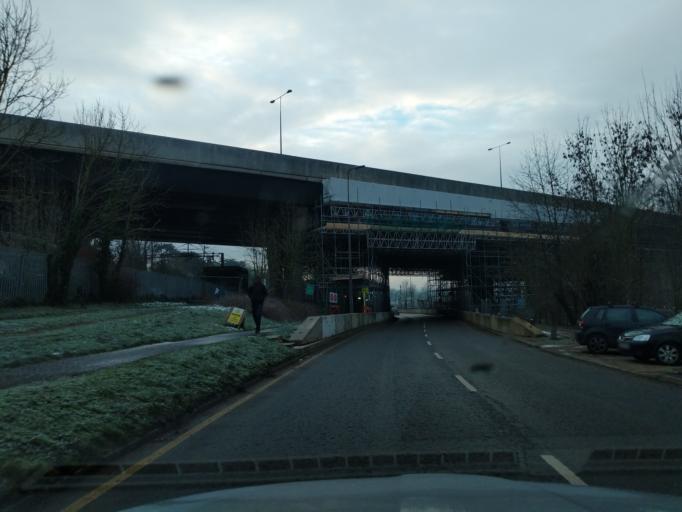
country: GB
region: England
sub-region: Hertfordshire
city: Kings Langley
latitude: 51.7055
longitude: -0.4382
